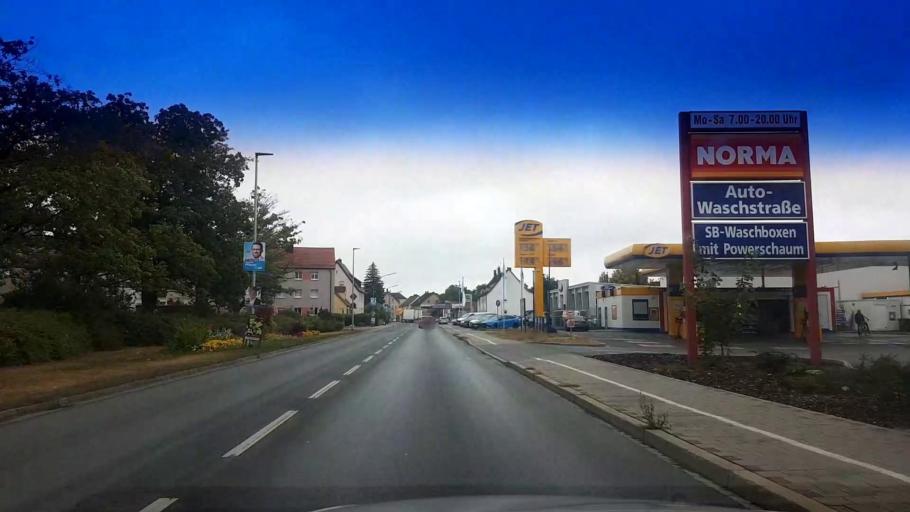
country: DE
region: Bavaria
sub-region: Upper Franconia
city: Forchheim
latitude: 49.7296
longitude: 11.0582
